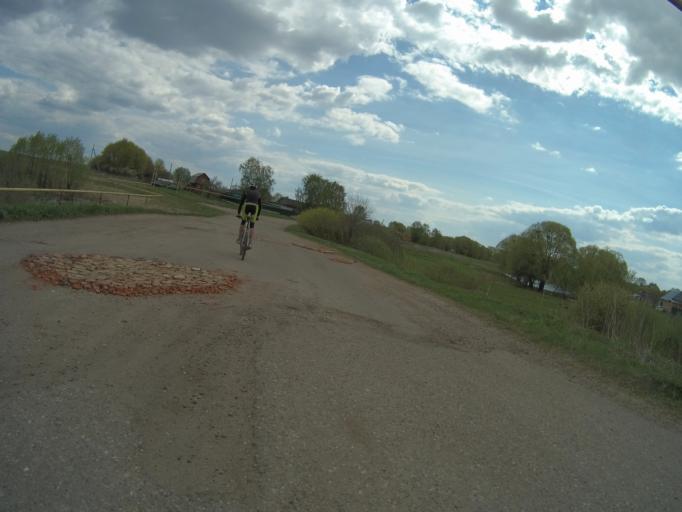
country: RU
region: Vladimir
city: Suzdal'
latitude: 56.3089
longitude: 40.2906
